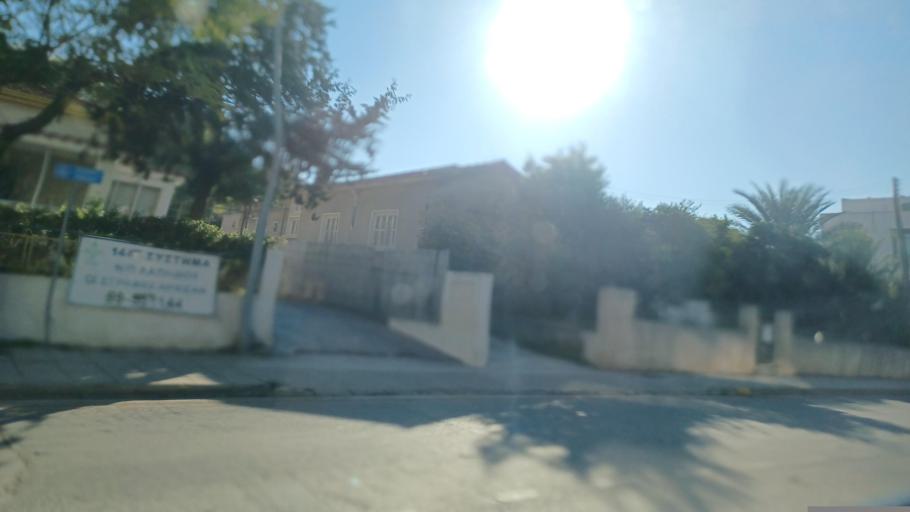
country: CY
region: Lefkosia
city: Nicosia
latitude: 35.1540
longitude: 33.3438
